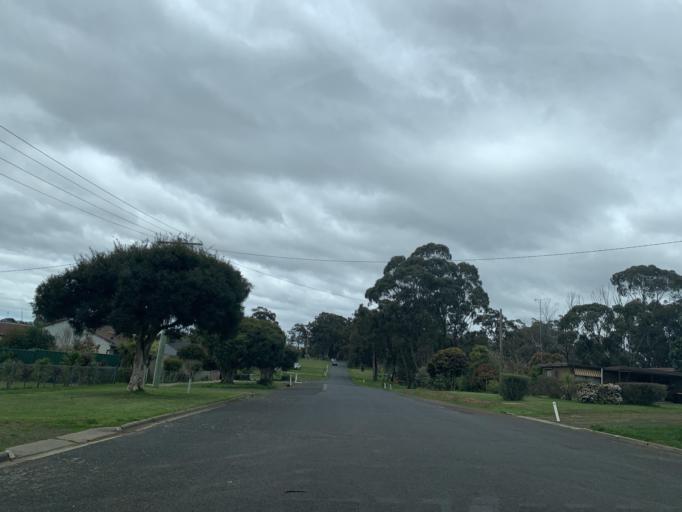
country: AU
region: Victoria
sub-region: Whittlesea
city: Whittlesea
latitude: -37.2103
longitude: 145.0401
